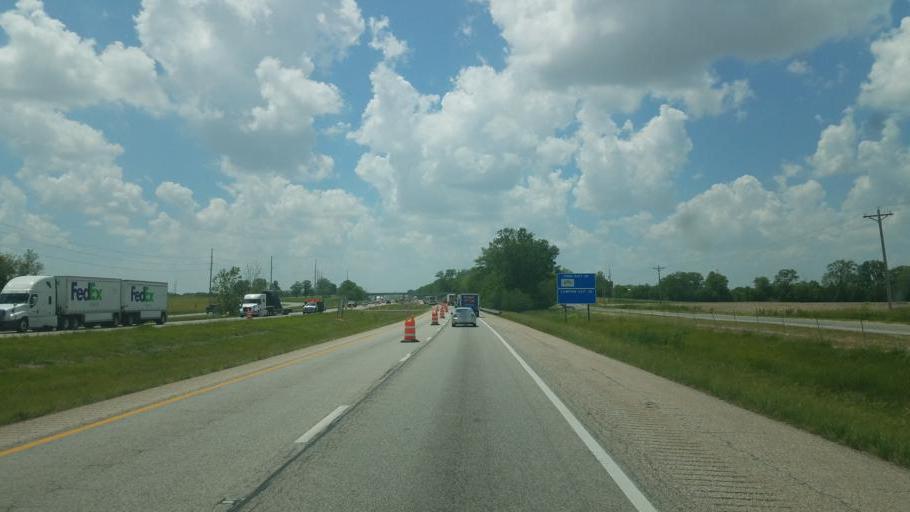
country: US
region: Illinois
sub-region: Madison County
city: Highland
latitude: 38.8047
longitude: -89.5934
